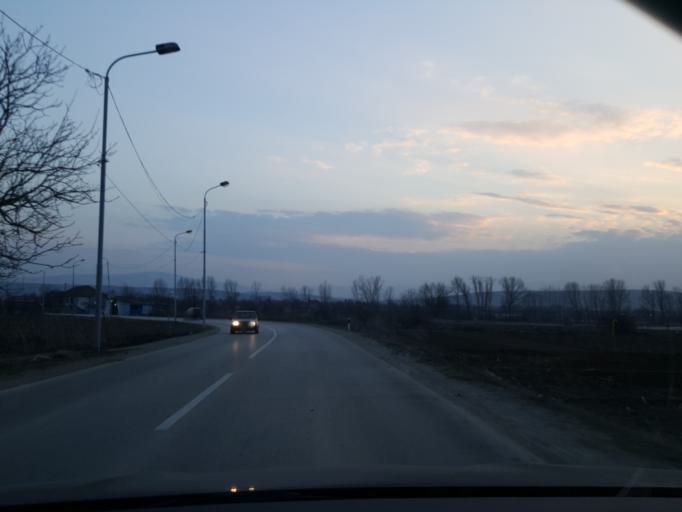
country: RS
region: Central Serbia
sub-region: Nisavski Okrug
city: Aleksinac
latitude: 43.5187
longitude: 21.6999
